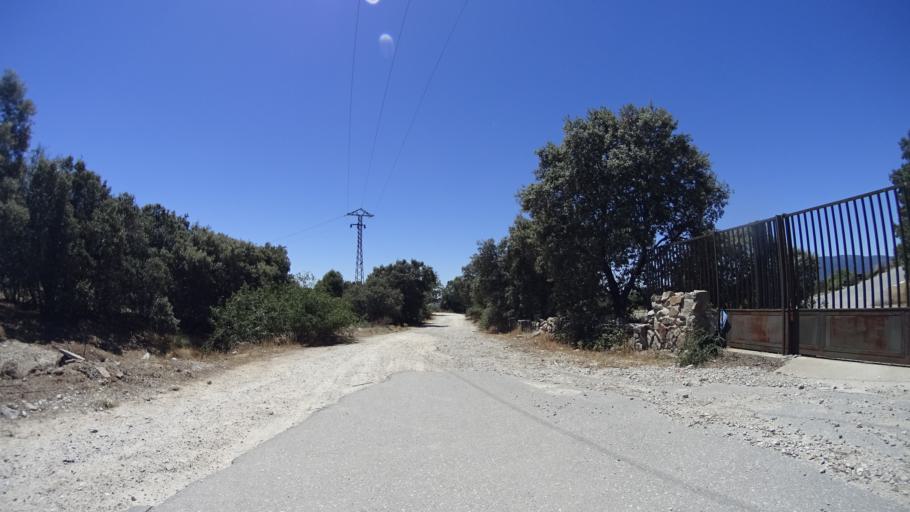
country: ES
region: Madrid
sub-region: Provincia de Madrid
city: Collado Mediano
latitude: 40.6800
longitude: -4.0139
